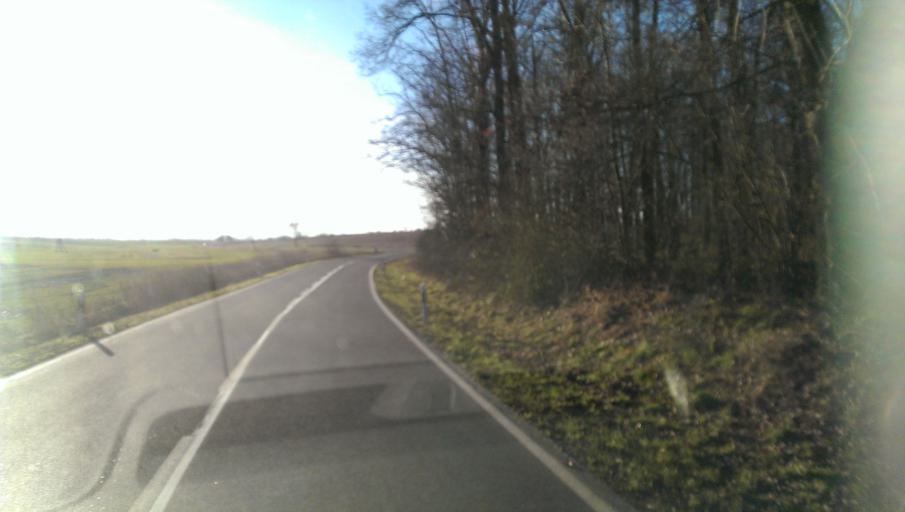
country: DE
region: Saxony-Anhalt
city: Eilsleben
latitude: 52.1071
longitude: 11.1852
